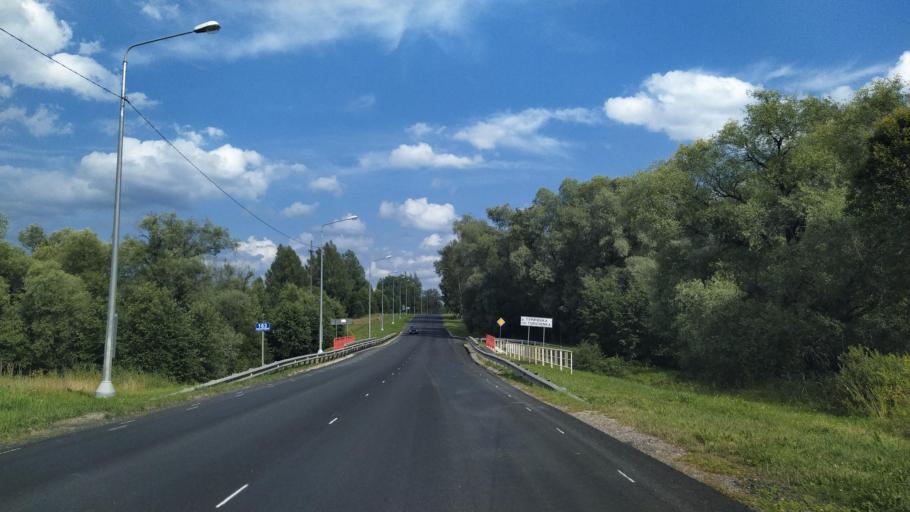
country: RU
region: Pskov
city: Porkhov
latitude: 57.7312
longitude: 29.3851
